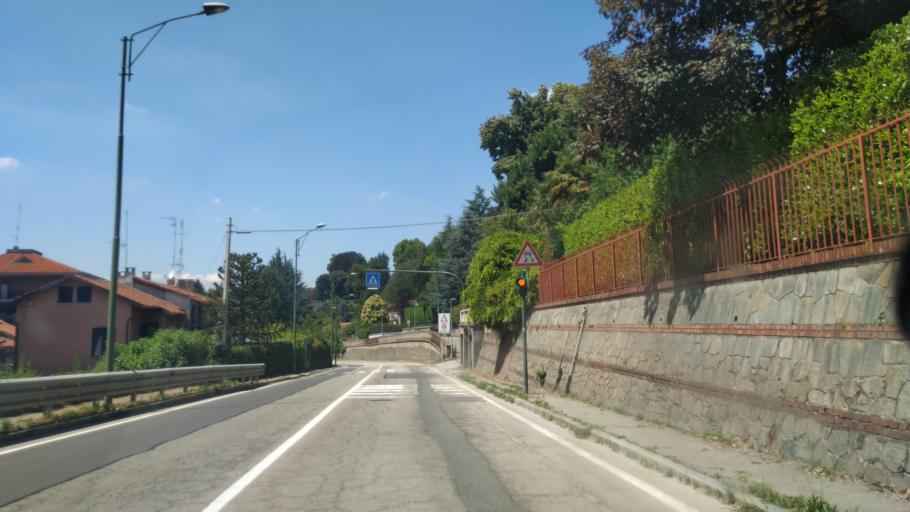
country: IT
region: Piedmont
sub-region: Provincia di Torino
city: San Mauro Torinese
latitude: 45.0801
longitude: 7.7364
